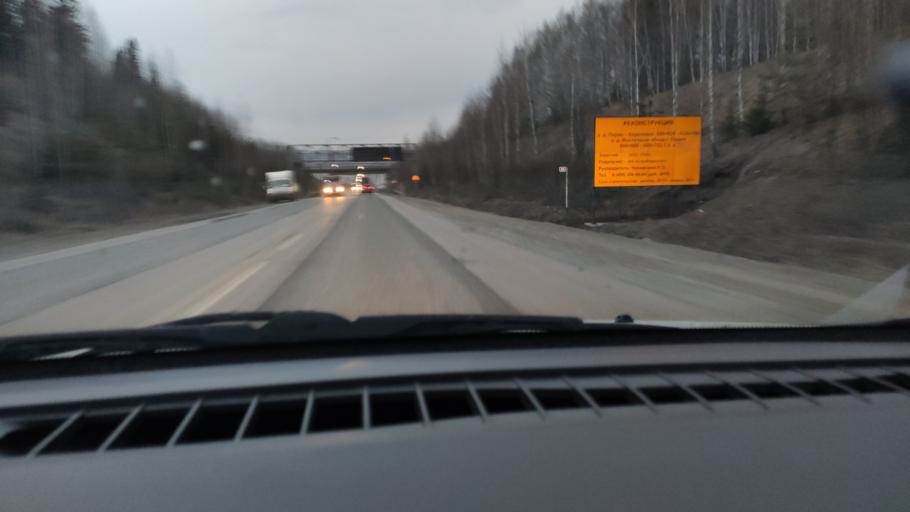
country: RU
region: Perm
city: Polazna
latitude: 58.1517
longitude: 56.4185
